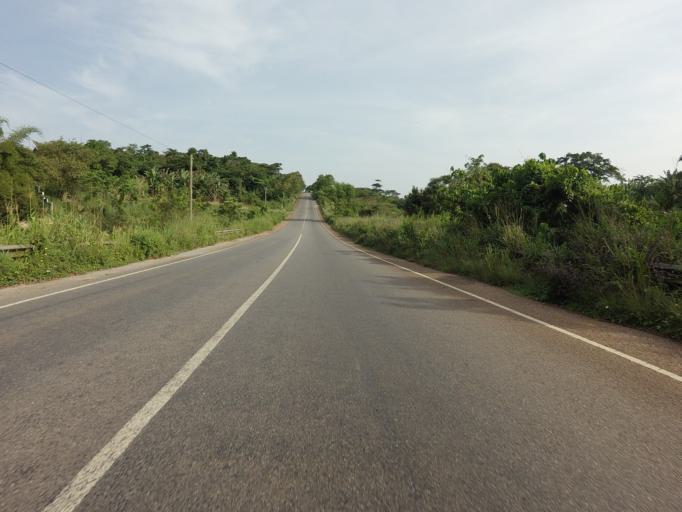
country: GH
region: Eastern
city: Aburi
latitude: 5.8787
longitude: -0.1556
